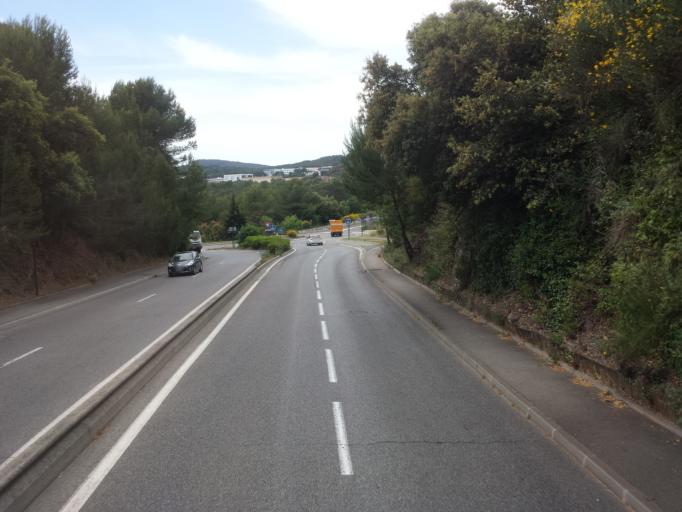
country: FR
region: Provence-Alpes-Cote d'Azur
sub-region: Departement des Alpes-Maritimes
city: Biot
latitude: 43.6131
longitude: 7.0791
